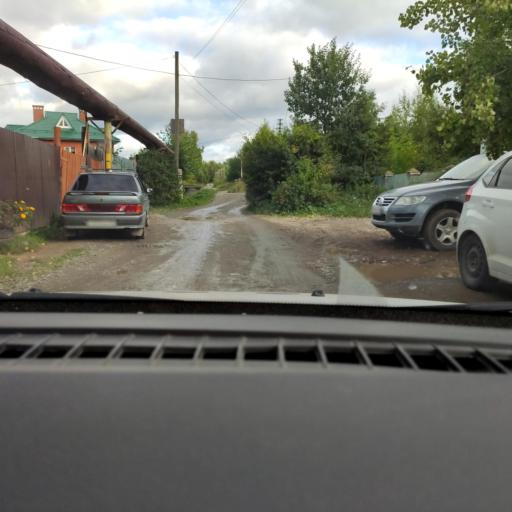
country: RU
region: Perm
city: Perm
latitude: 58.1135
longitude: 56.3935
